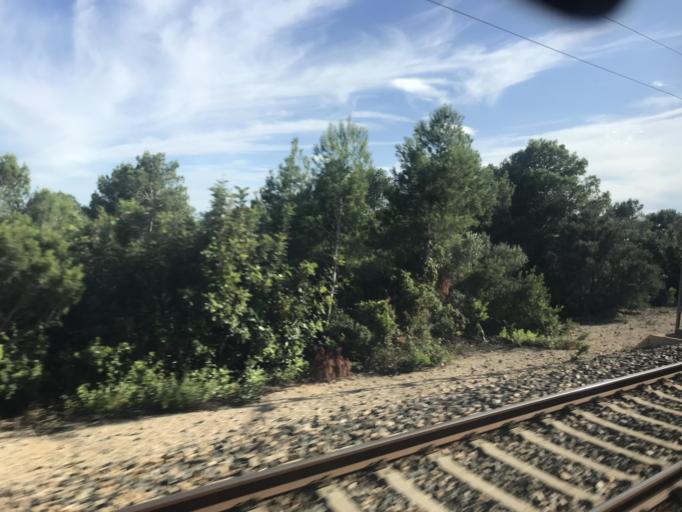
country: ES
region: Catalonia
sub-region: Provincia de Tarragona
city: l'Ametlla de Mar
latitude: 40.8551
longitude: 0.7652
